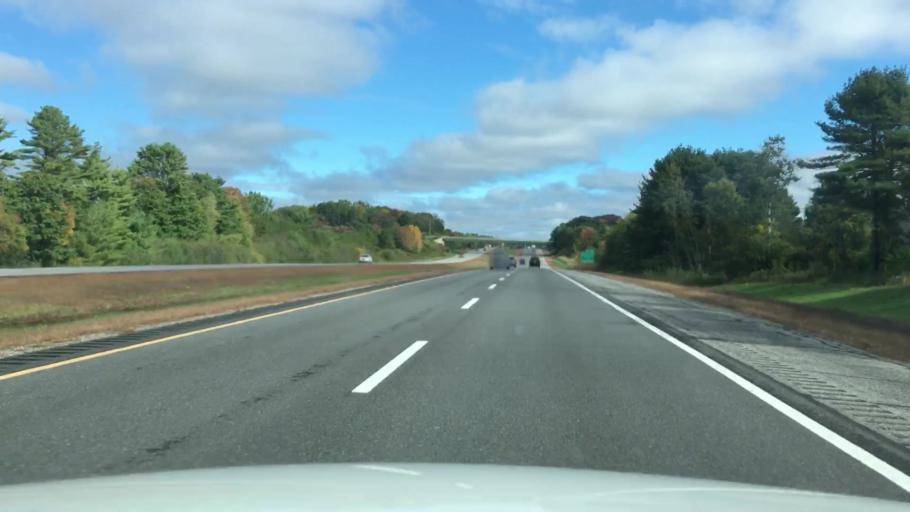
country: US
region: Maine
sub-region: Cumberland County
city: Freeport
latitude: 43.8257
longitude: -70.1384
